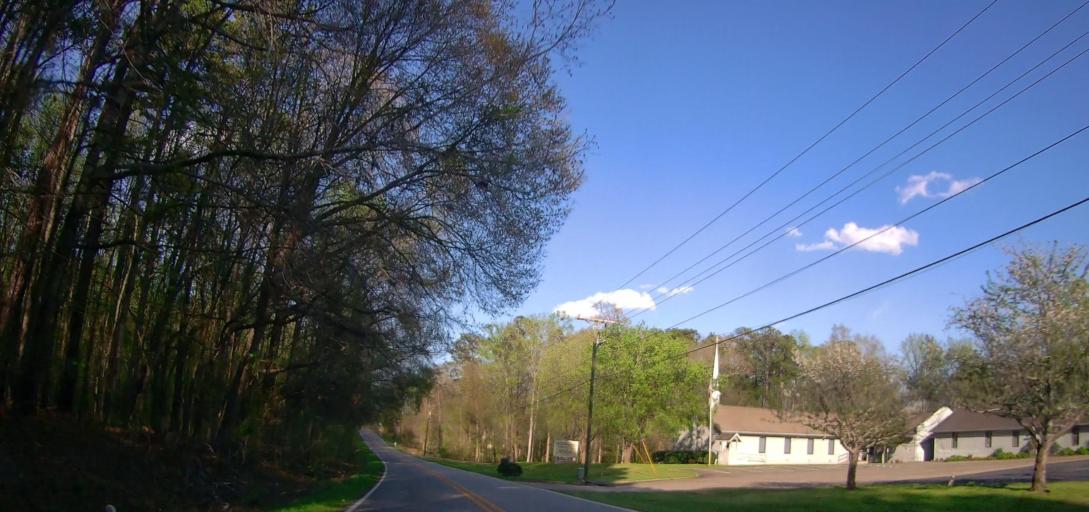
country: US
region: Georgia
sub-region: Putnam County
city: Eatonton
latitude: 33.1995
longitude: -83.3852
